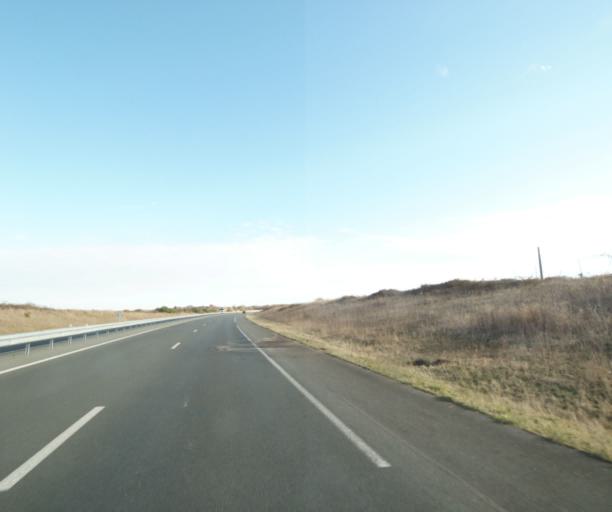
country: FR
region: Poitou-Charentes
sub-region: Departement de la Charente-Maritime
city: Saint-Romain-de-Benet
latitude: 45.6935
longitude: -0.8255
